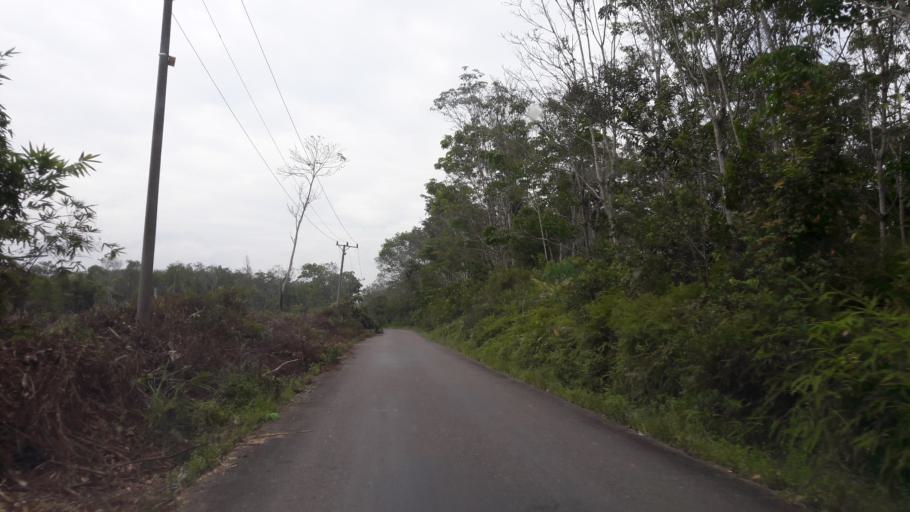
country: ID
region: South Sumatra
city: Gunungmenang
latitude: -3.1236
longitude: 104.1147
